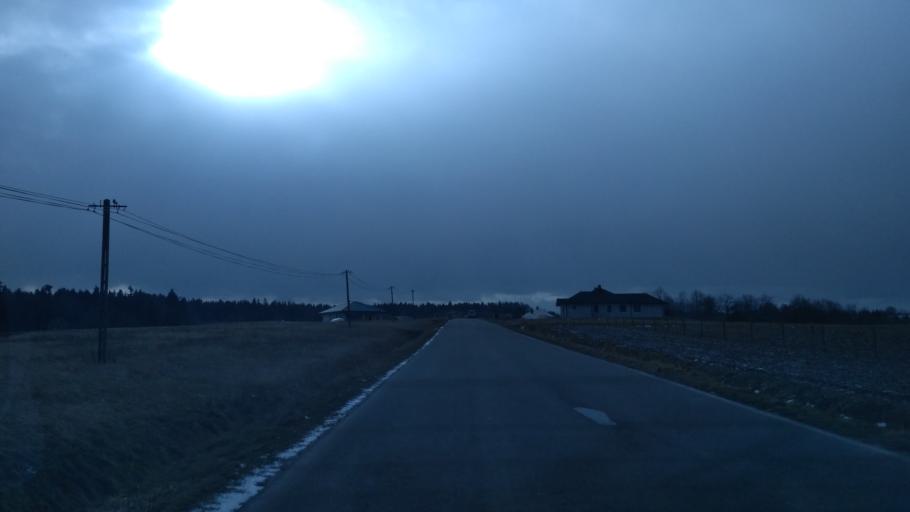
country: PL
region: Subcarpathian Voivodeship
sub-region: Powiat rzeszowski
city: Blazowa
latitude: 49.8453
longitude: 22.0884
